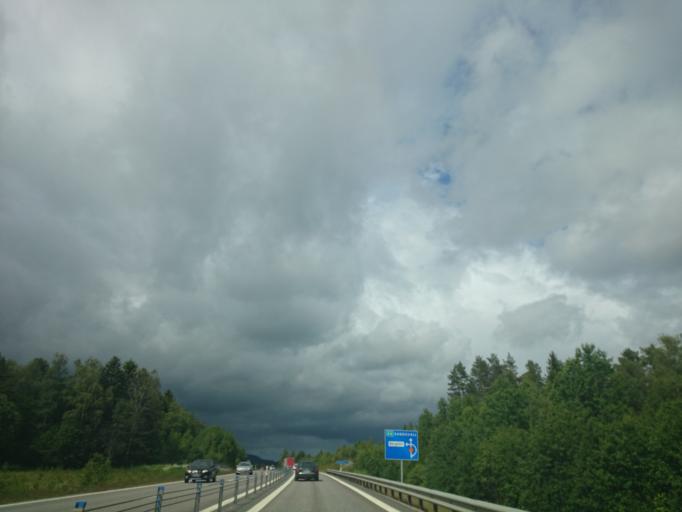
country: SE
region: Vaesternorrland
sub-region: Sundsvalls Kommun
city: Njurundabommen
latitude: 62.2352
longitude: 17.3749
